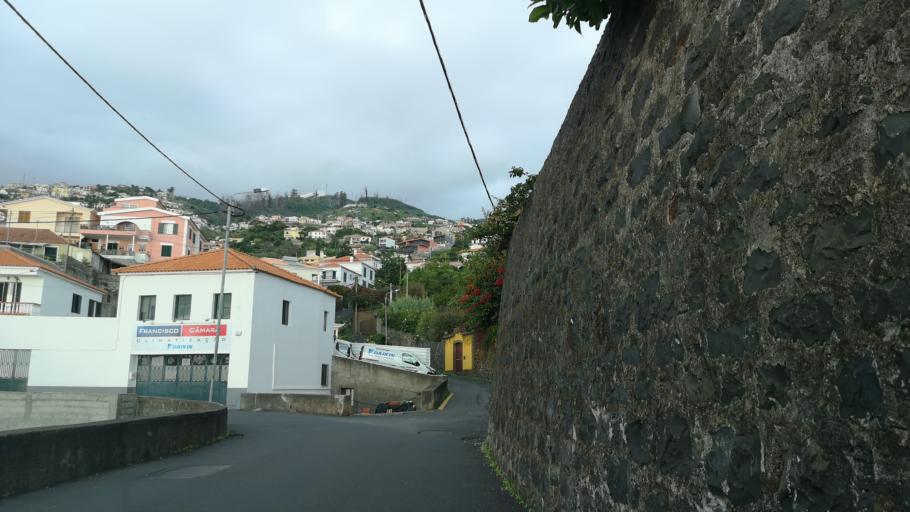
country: PT
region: Madeira
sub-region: Funchal
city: Nossa Senhora do Monte
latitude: 32.6561
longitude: -16.8944
